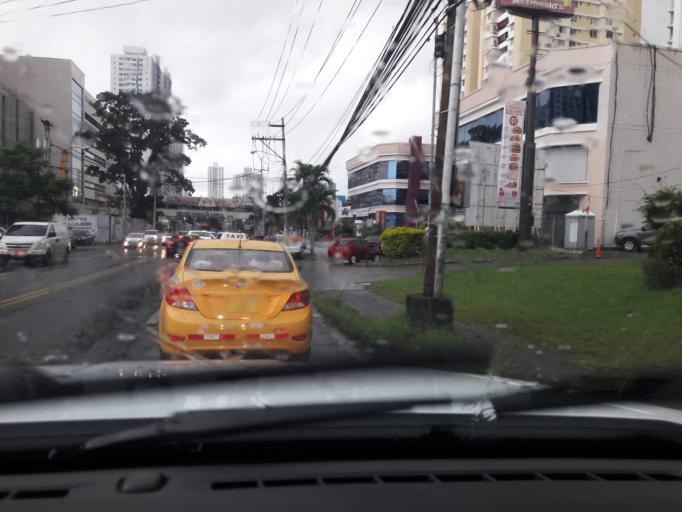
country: PA
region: Panama
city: Panama
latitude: 9.0024
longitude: -79.5162
